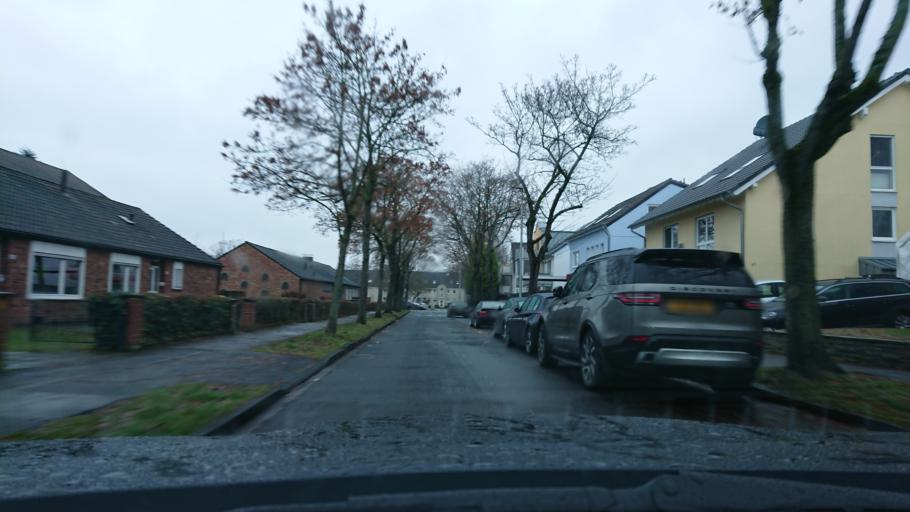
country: DE
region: North Rhine-Westphalia
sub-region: Regierungsbezirk Koln
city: Siegburg
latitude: 50.8046
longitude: 7.1906
